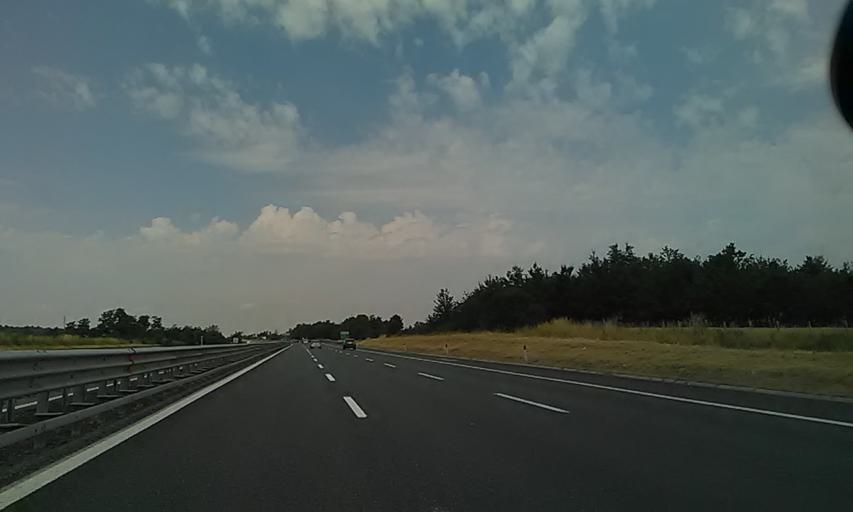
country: IT
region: Piedmont
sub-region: Provincia di Alessandria
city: Predosa
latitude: 44.7297
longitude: 8.6640
